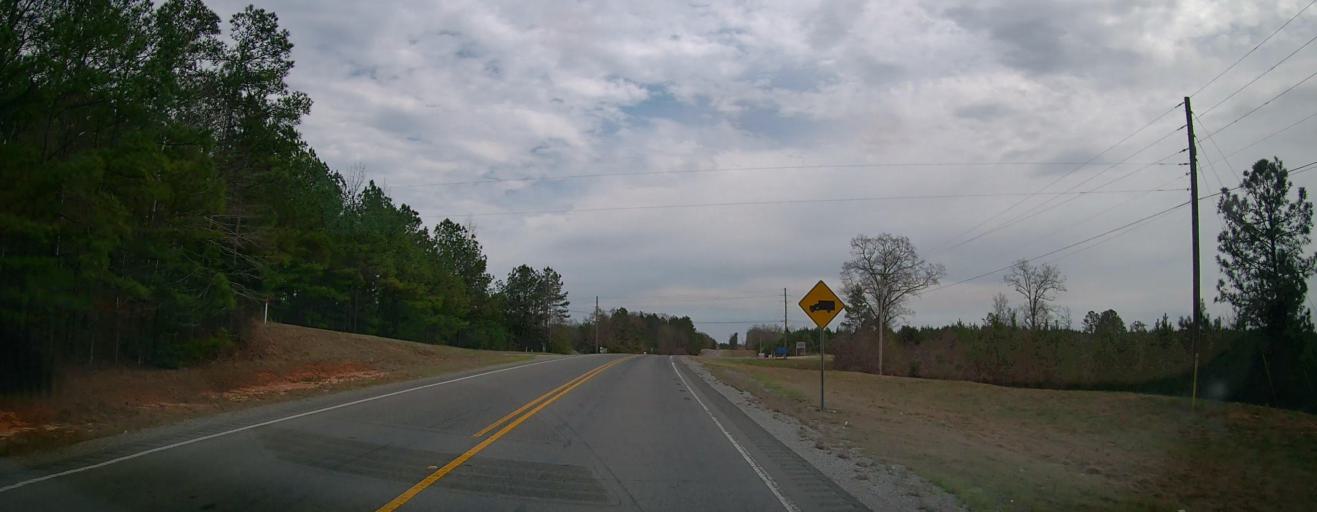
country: US
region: Alabama
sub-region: Marion County
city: Guin
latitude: 34.0395
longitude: -87.9519
